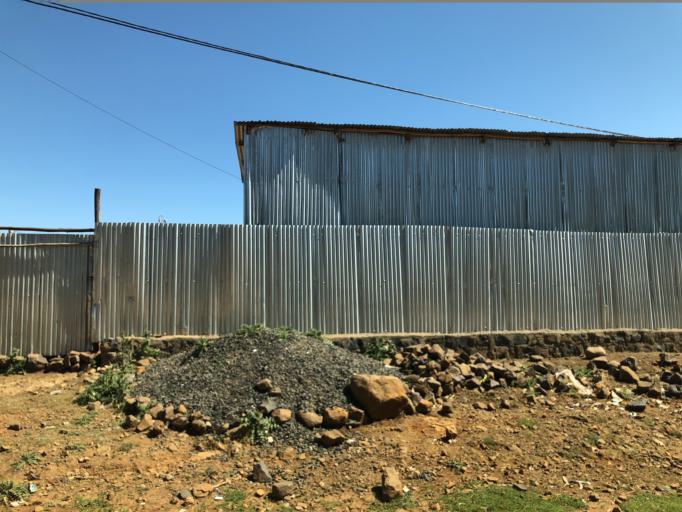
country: ET
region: Amhara
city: Lalibela
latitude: 11.6905
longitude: 38.9224
